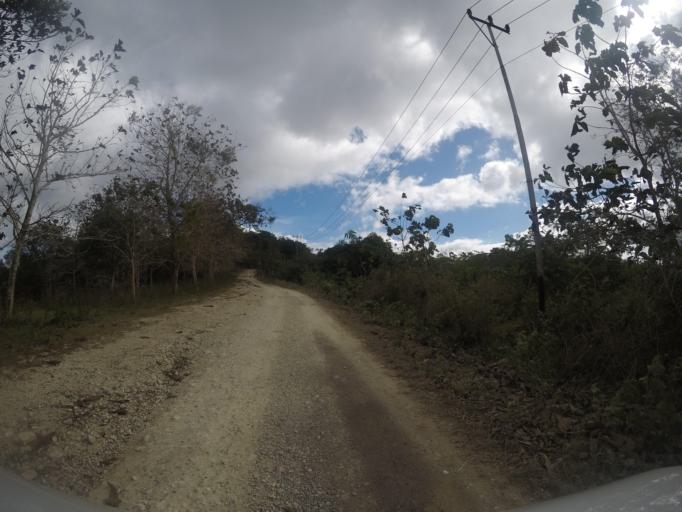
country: TL
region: Lautem
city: Lospalos
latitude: -8.5466
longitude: 126.9034
